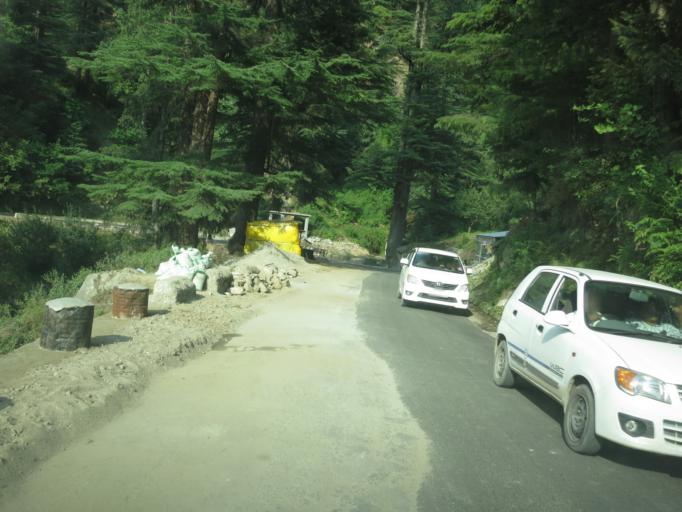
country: IN
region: Himachal Pradesh
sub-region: Kulu
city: Nagar
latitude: 32.1758
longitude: 77.1958
